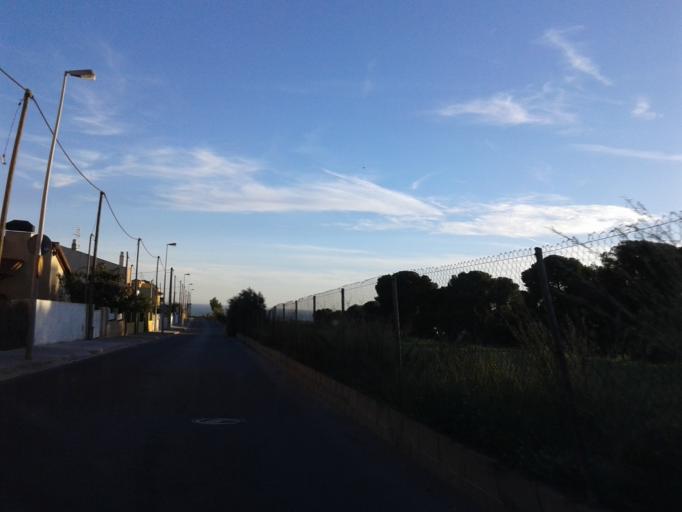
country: ES
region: Catalonia
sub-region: Provincia de Barcelona
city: Cubelles
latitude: 41.2279
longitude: 1.6918
